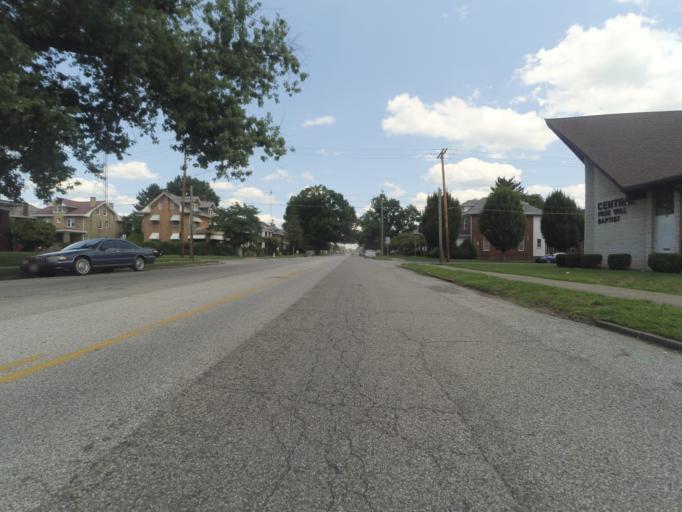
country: US
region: West Virginia
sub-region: Cabell County
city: Huntington
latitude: 38.4167
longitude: -82.4503
